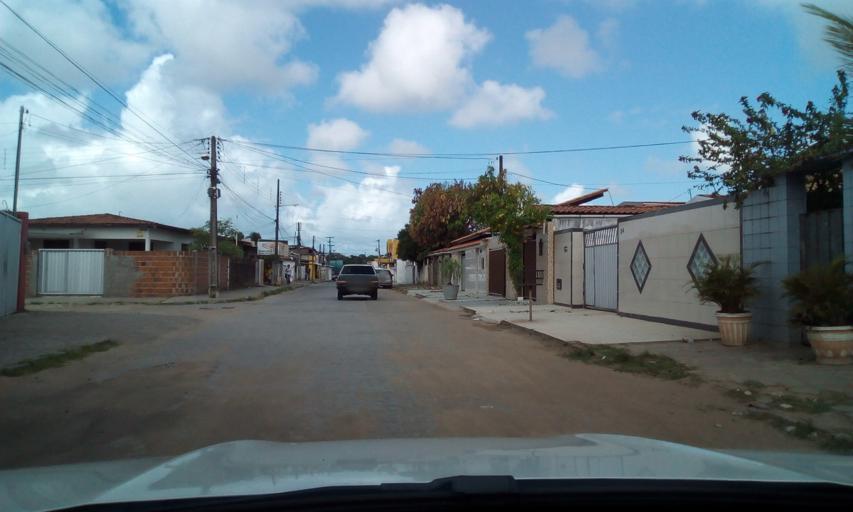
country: BR
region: Paraiba
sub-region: Joao Pessoa
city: Joao Pessoa
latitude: -7.1528
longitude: -34.8740
